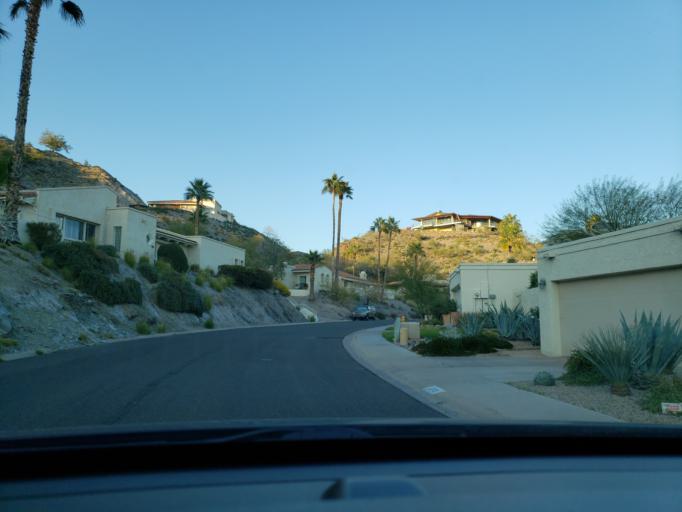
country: US
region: Arizona
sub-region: Maricopa County
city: Paradise Valley
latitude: 33.5501
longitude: -112.0458
